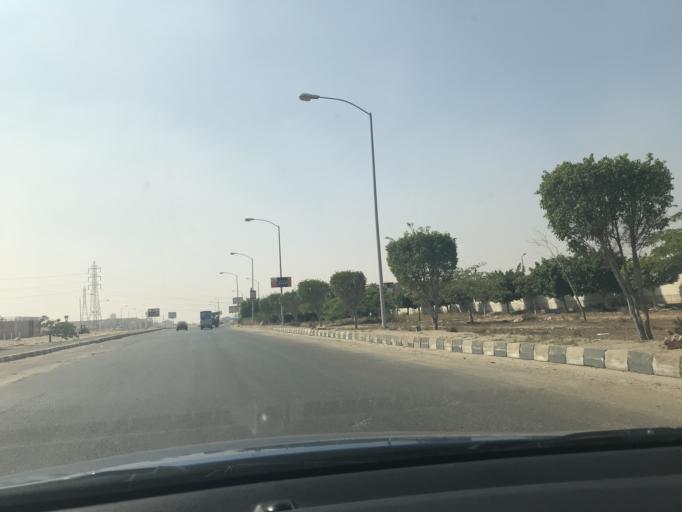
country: EG
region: Eastern Province
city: Bilbays
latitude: 30.2497
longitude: 31.7598
